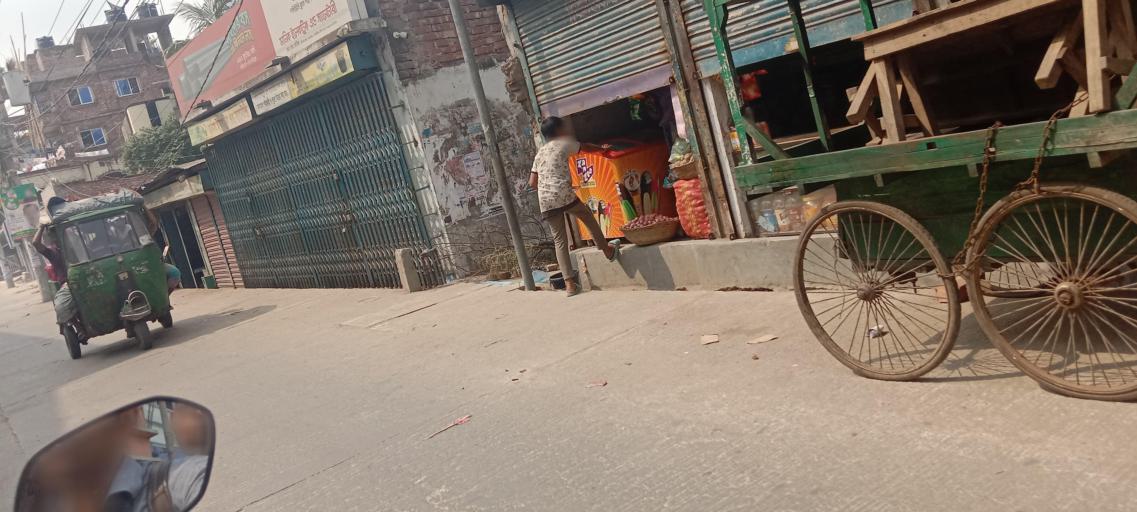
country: BD
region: Dhaka
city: Azimpur
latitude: 23.7143
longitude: 90.3570
